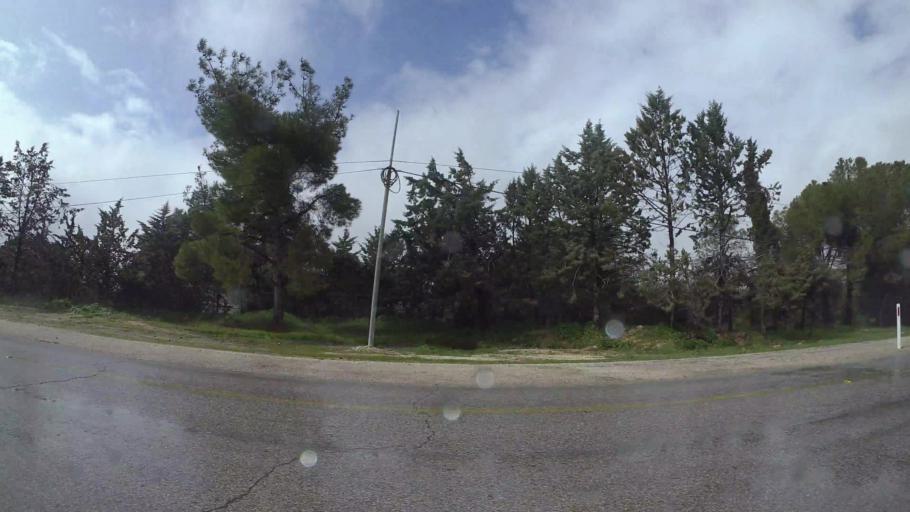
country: JO
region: Amman
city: Al Jubayhah
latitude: 32.0227
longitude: 35.8180
